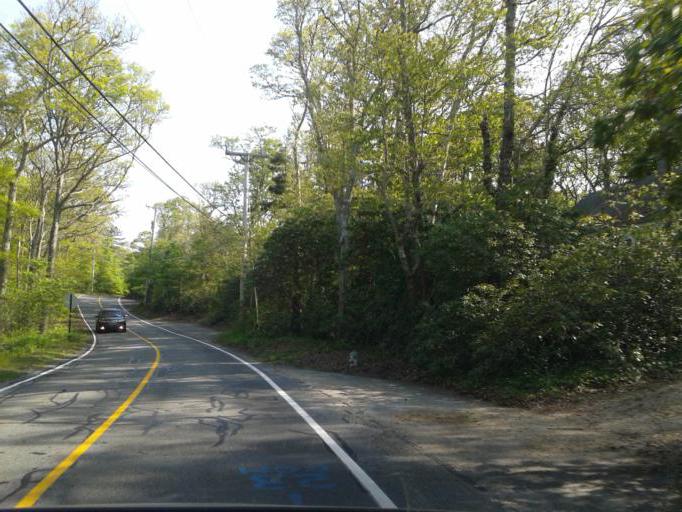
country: US
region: Massachusetts
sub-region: Barnstable County
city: Falmouth
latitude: 41.5262
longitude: -70.6541
